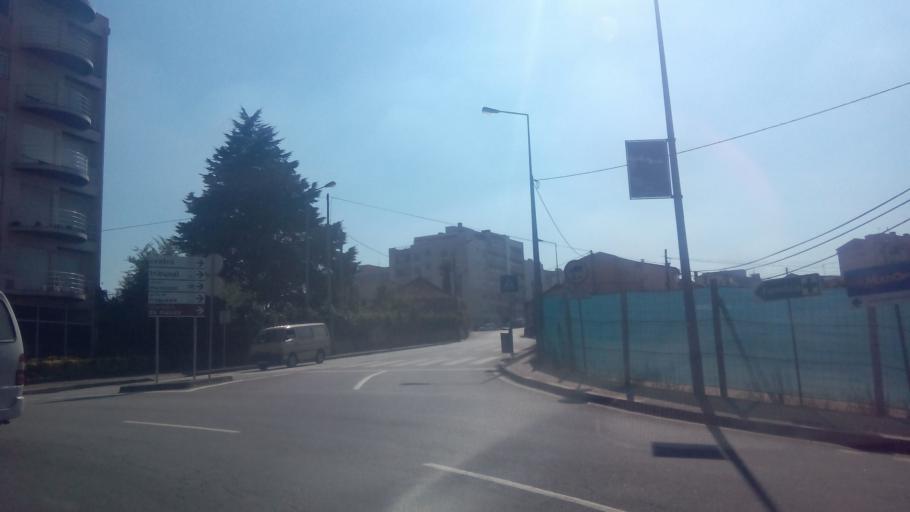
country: PT
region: Porto
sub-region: Paredes
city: Paredes
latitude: 41.2098
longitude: -8.3283
